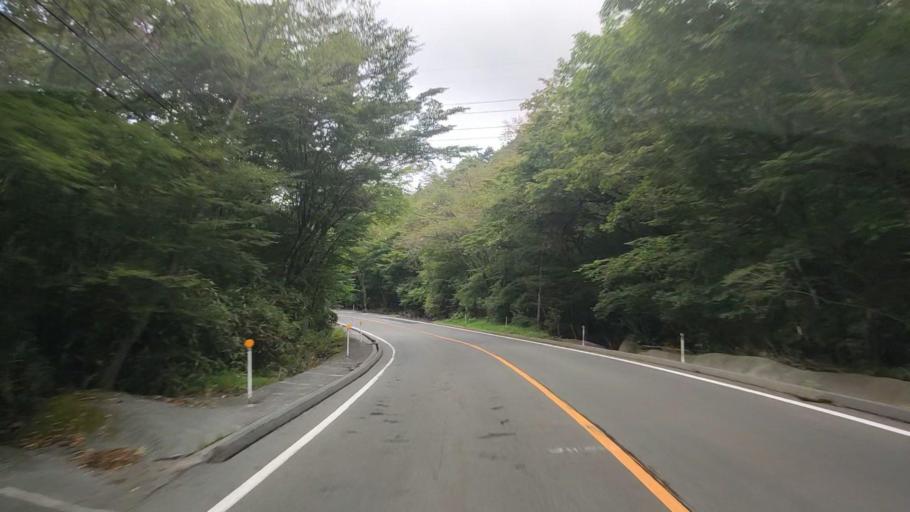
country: JP
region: Shizuoka
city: Fuji
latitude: 35.2800
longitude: 138.7828
